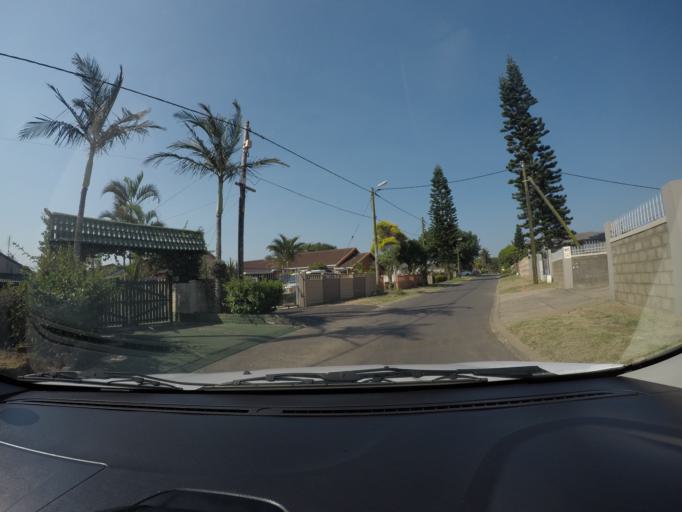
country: ZA
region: KwaZulu-Natal
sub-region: uThungulu District Municipality
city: Richards Bay
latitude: -28.7161
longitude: 32.0412
